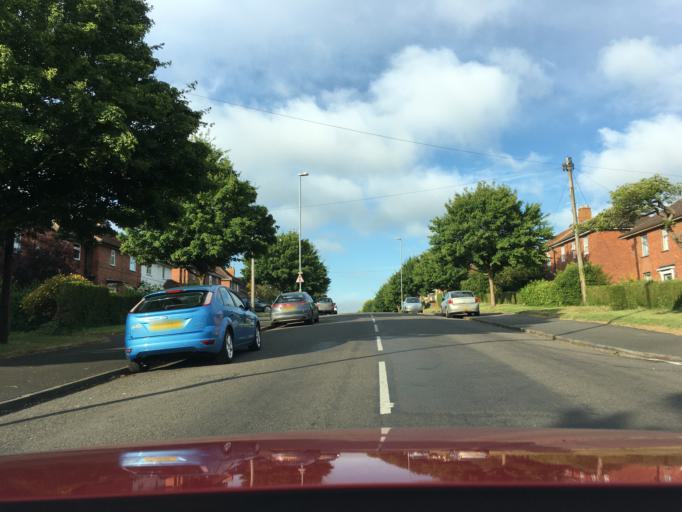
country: GB
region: England
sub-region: North Somerset
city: Easton-in-Gordano
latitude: 51.4905
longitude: -2.6498
